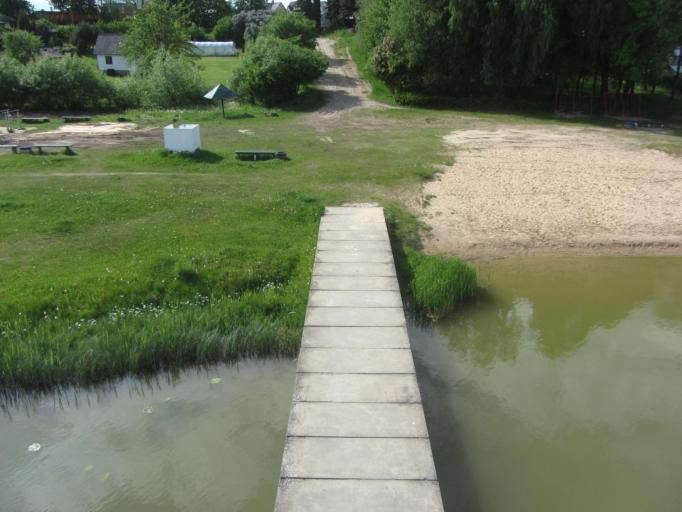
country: LT
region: Utenos apskritis
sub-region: Utena
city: Utena
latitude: 55.4928
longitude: 25.5900
